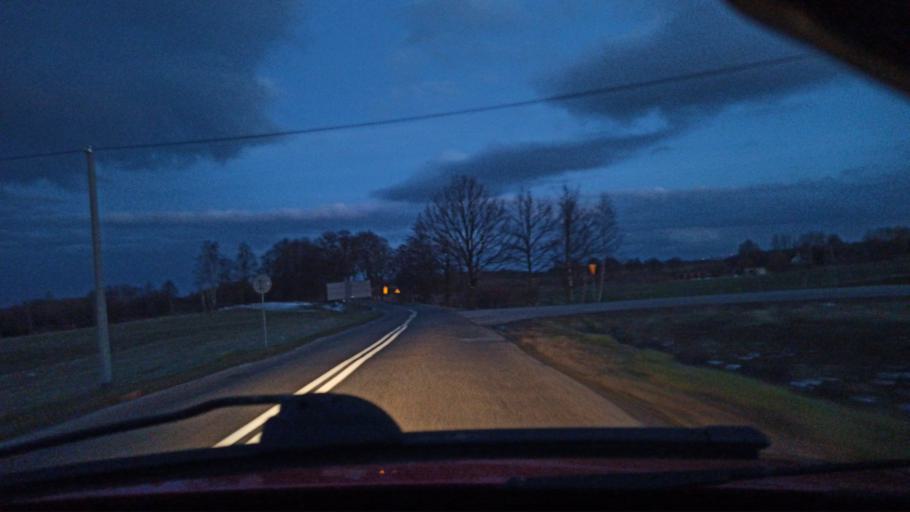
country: PL
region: Warmian-Masurian Voivodeship
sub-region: Powiat elblaski
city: Gronowo Gorne
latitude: 54.1682
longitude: 19.5318
